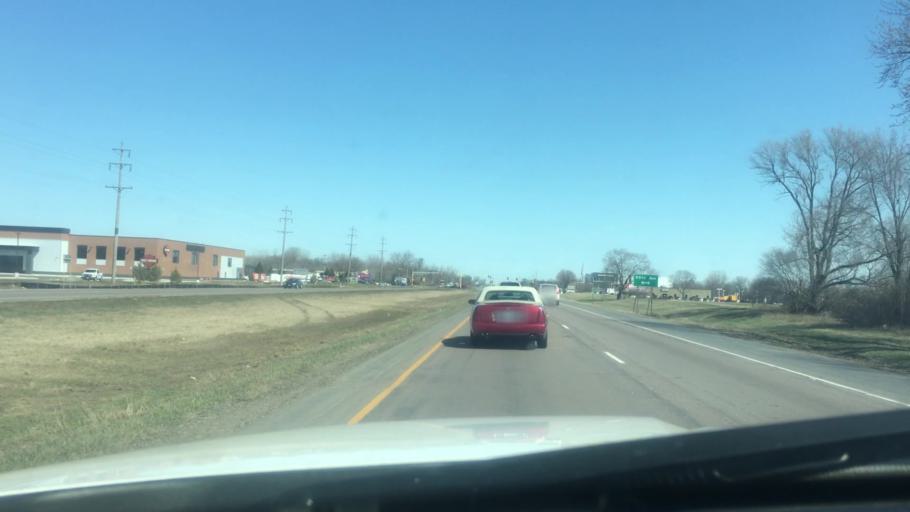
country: US
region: Minnesota
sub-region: Anoka County
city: Blaine
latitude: 45.1465
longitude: -93.2352
